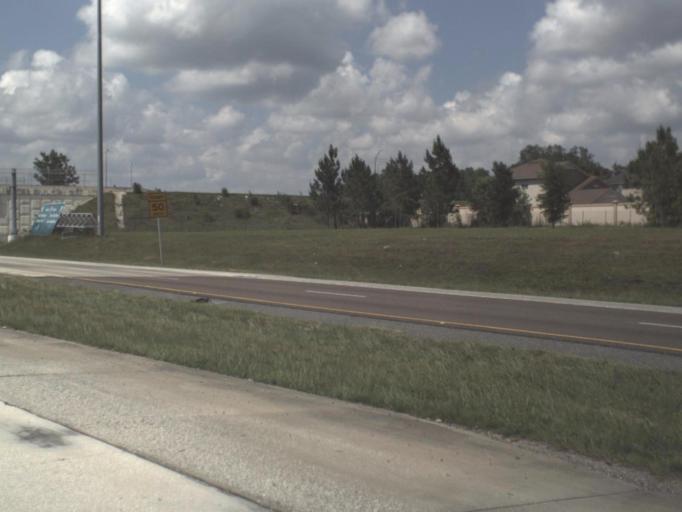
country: US
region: Florida
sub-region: Saint Johns County
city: Fruit Cove
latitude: 30.1604
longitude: -81.5514
